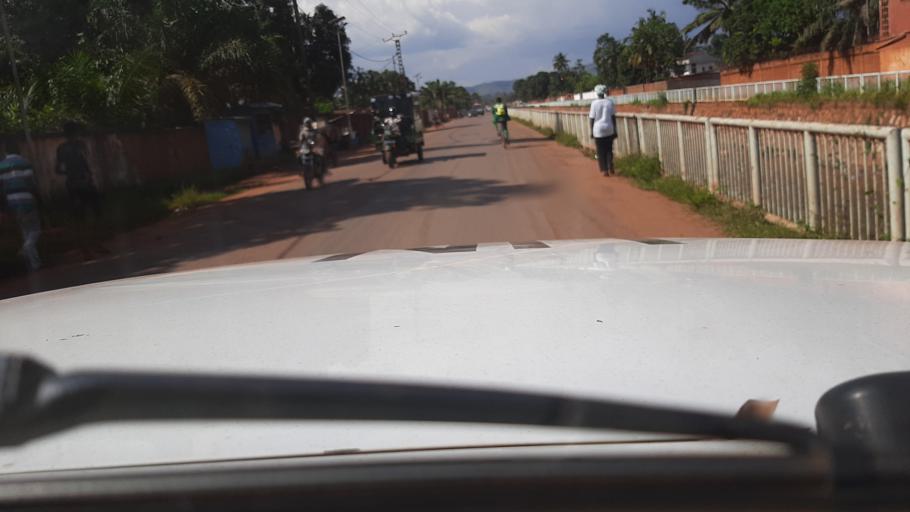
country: CF
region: Bangui
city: Bangui
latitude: 4.3706
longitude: 18.5523
